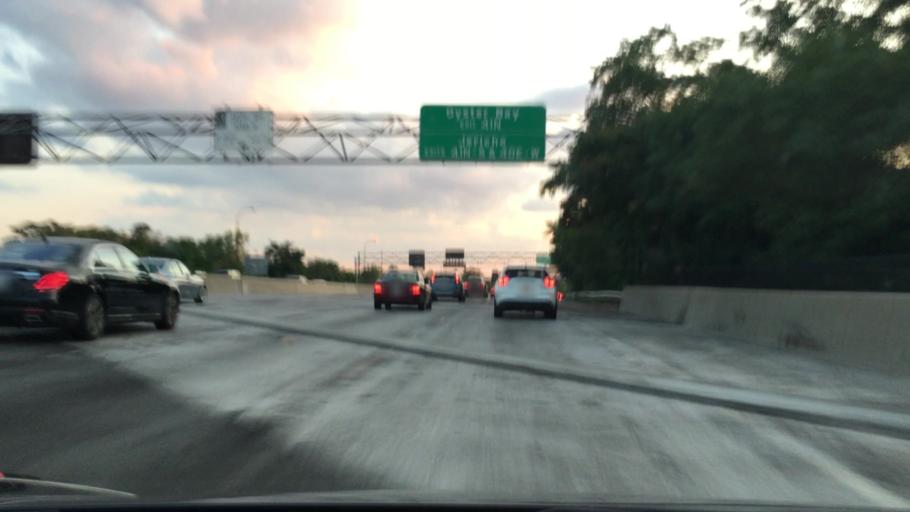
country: US
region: New York
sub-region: Nassau County
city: Jericho
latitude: 40.7872
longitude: -73.5278
